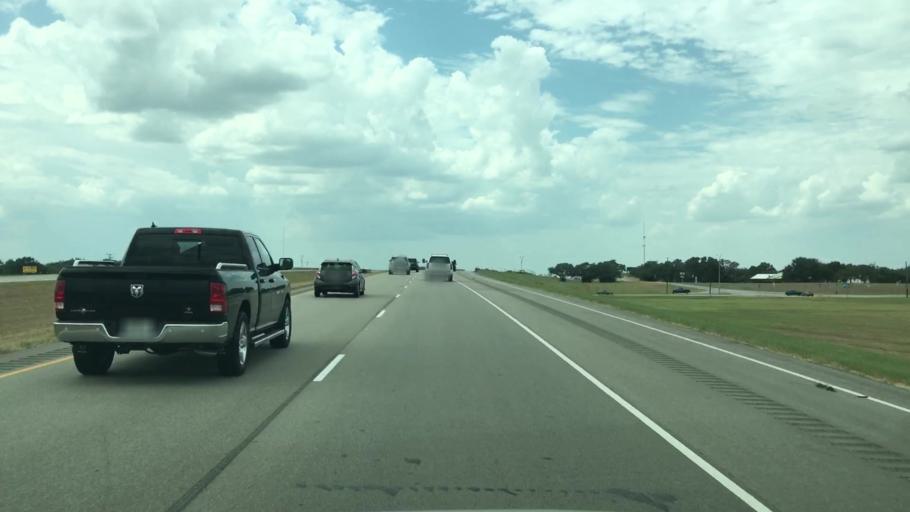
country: US
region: Texas
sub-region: Live Oak County
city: Three Rivers
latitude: 28.4877
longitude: -98.1407
